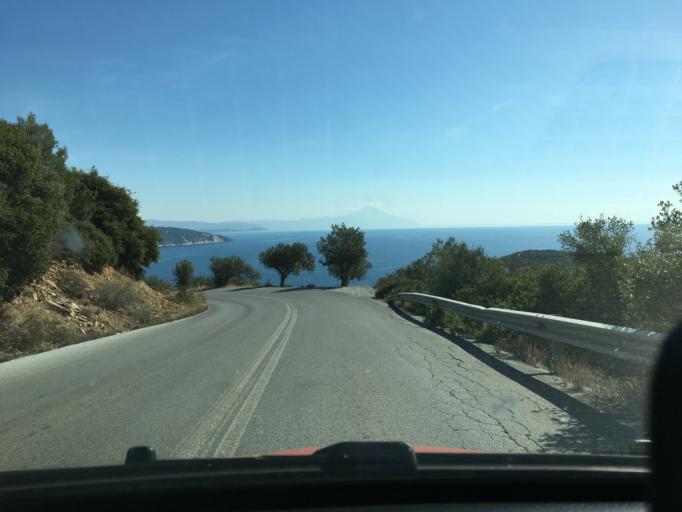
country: GR
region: Central Macedonia
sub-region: Nomos Chalkidikis
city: Agios Nikolaos
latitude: 40.3447
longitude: 23.7158
